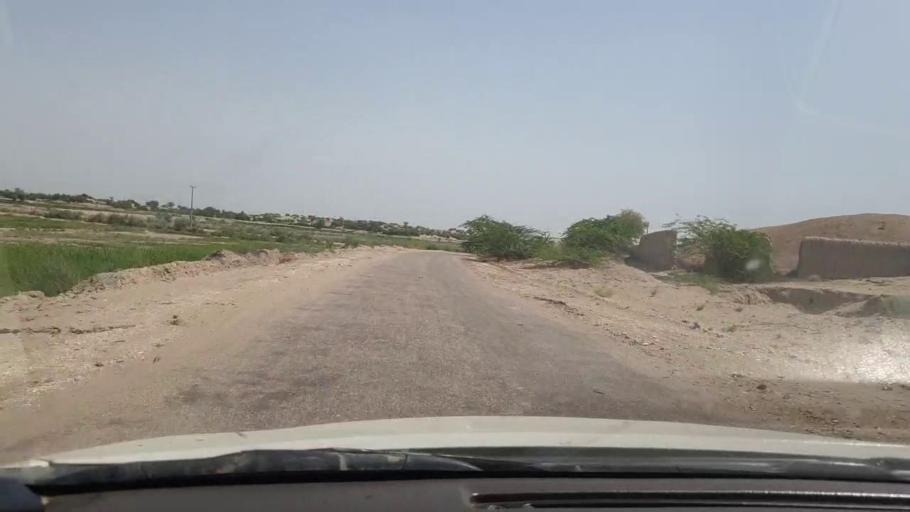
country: PK
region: Sindh
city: Rohri
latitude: 27.4838
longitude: 69.0550
